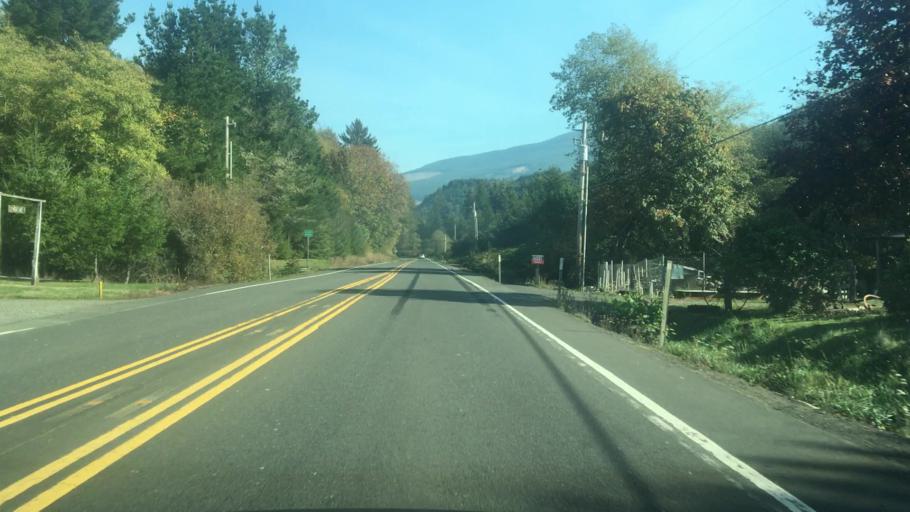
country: US
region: Oregon
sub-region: Lincoln County
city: Rose Lodge
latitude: 45.0212
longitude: -123.8544
